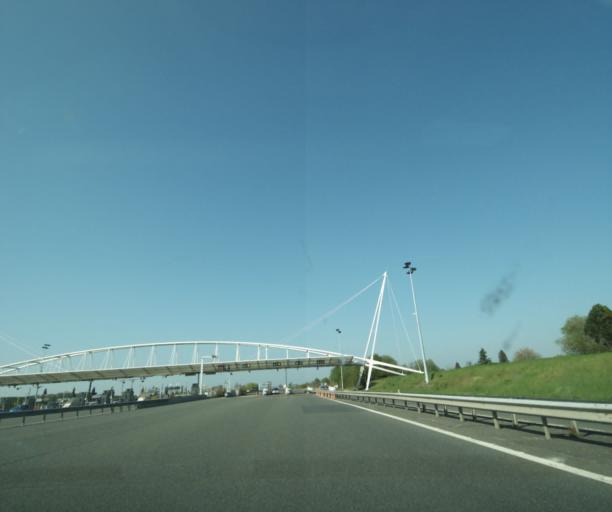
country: FR
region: Ile-de-France
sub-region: Departement de Seine-et-Marne
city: Souppes-sur-Loing
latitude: 48.1755
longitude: 2.7672
